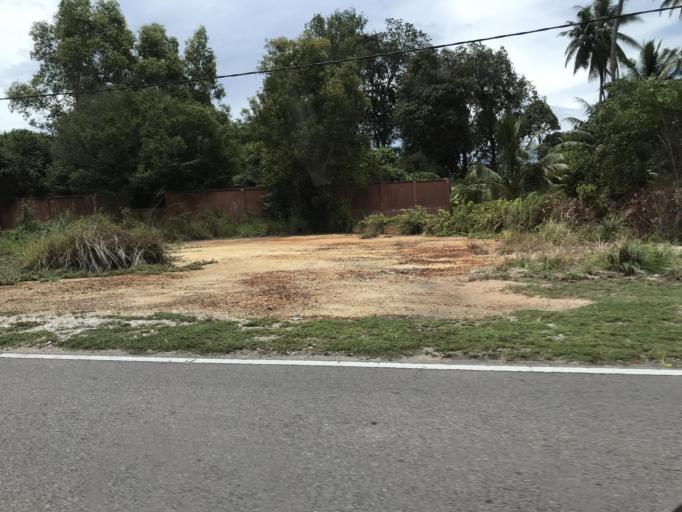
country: MY
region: Kelantan
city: Tumpat
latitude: 6.1741
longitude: 102.2008
